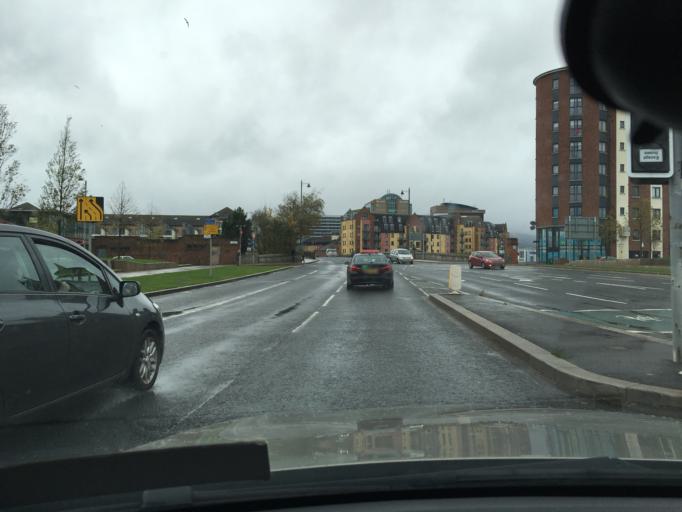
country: GB
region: Northern Ireland
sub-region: City of Belfast
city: Belfast
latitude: 54.5957
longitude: -5.9107
